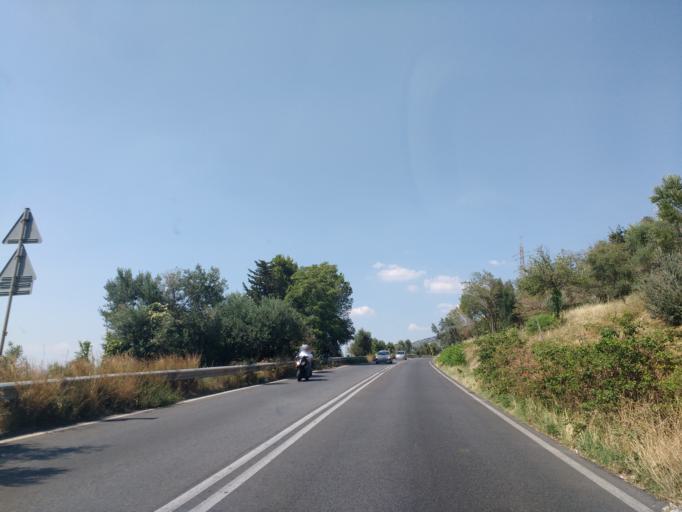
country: IT
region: Latium
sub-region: Citta metropolitana di Roma Capitale
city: Tivoli
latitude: 41.9509
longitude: 12.7910
